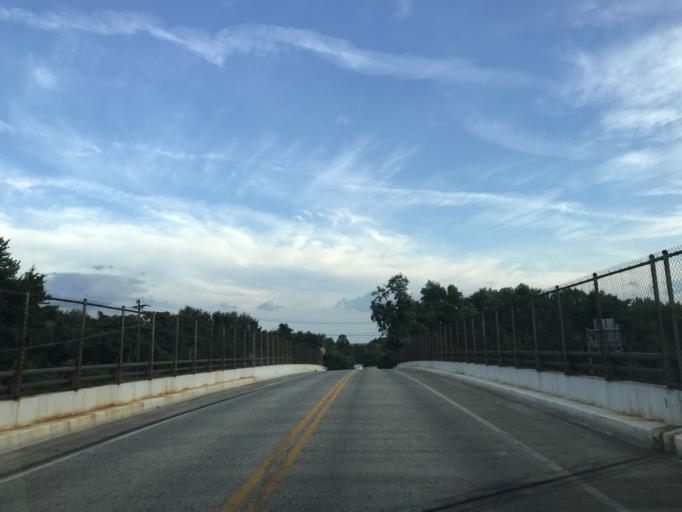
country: US
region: Maryland
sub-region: Harford County
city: Aberdeen
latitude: 39.5136
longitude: -76.2069
